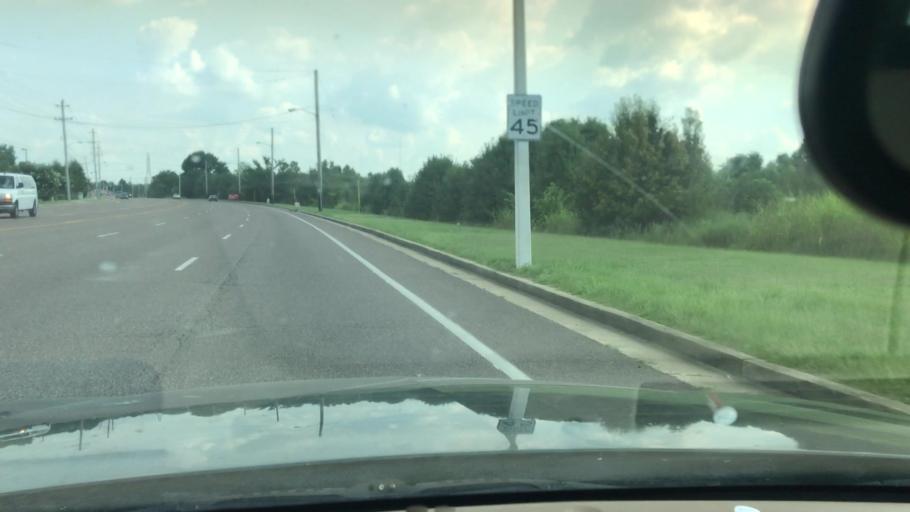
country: US
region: Tennessee
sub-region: Shelby County
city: Bartlett
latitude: 35.1935
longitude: -89.8151
